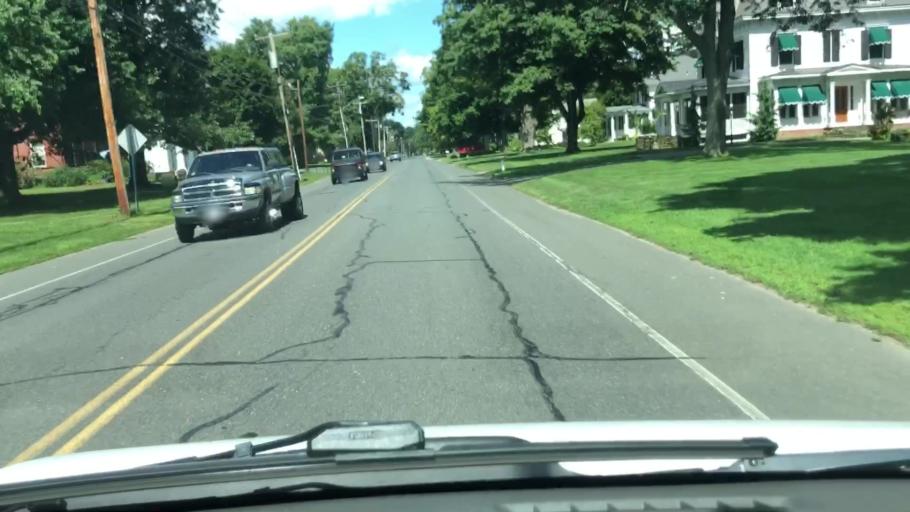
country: US
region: Massachusetts
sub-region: Hampshire County
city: Hatfield
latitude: 42.3693
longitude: -72.5968
